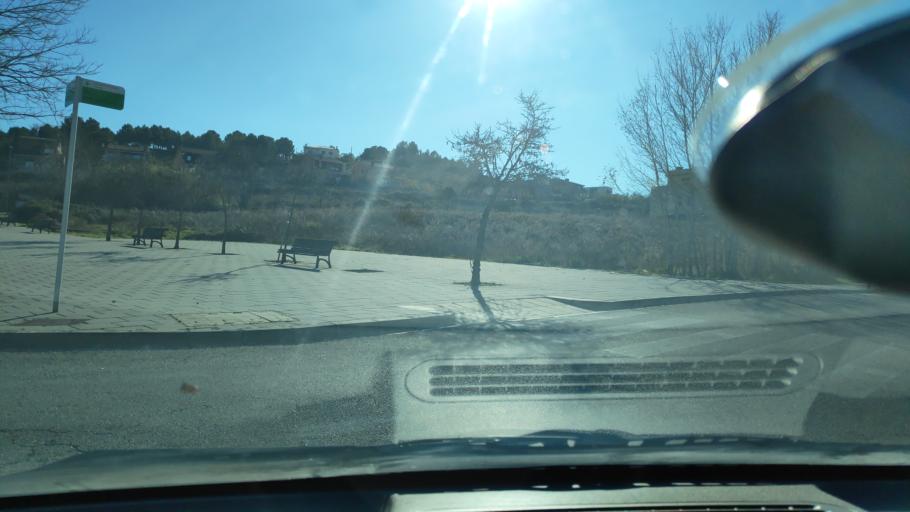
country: ES
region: Catalonia
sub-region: Provincia de Barcelona
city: Sant Quirze del Valles
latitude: 41.5272
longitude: 2.0783
